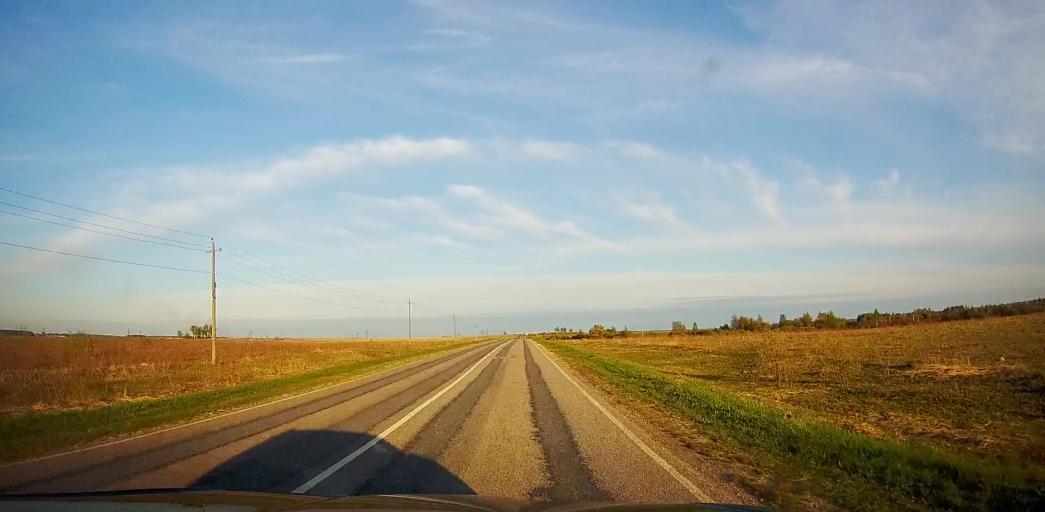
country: RU
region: Moskovskaya
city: Meshcherino
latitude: 55.2730
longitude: 38.2329
